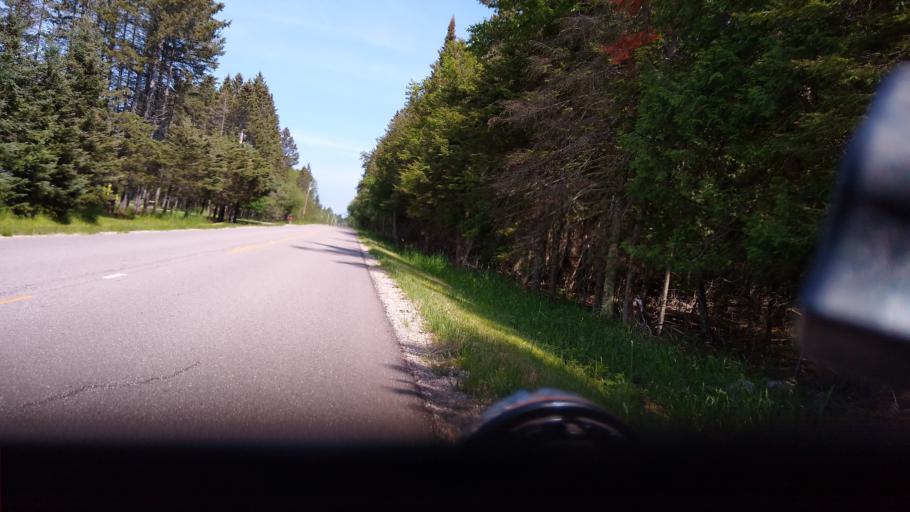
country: US
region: Michigan
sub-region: Delta County
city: Escanaba
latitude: 45.7101
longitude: -87.1299
